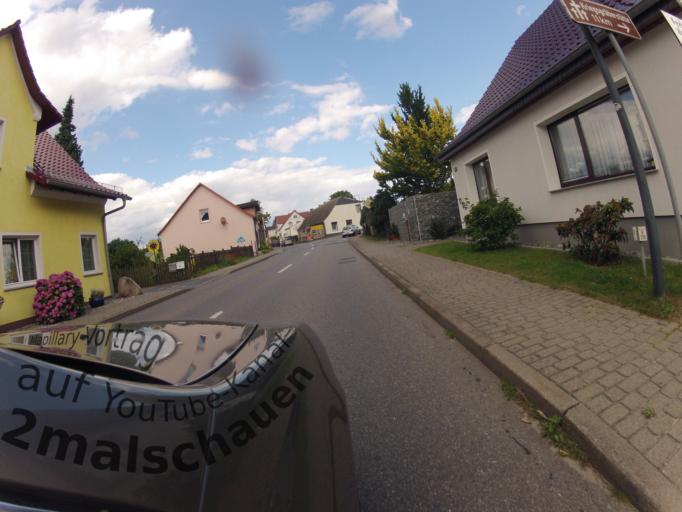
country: DE
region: Mecklenburg-Vorpommern
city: Seebad Heringsdorf
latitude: 53.8910
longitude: 14.1399
